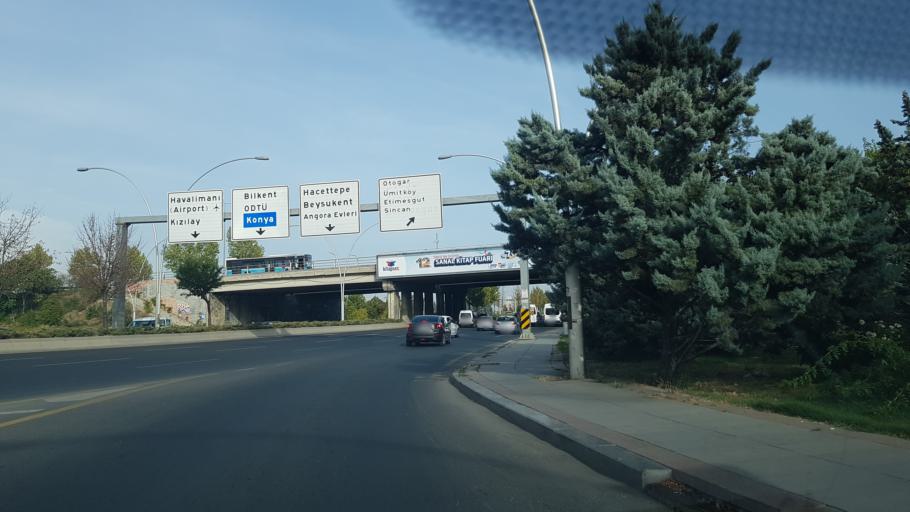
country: TR
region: Ankara
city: Batikent
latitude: 39.9053
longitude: 32.7098
